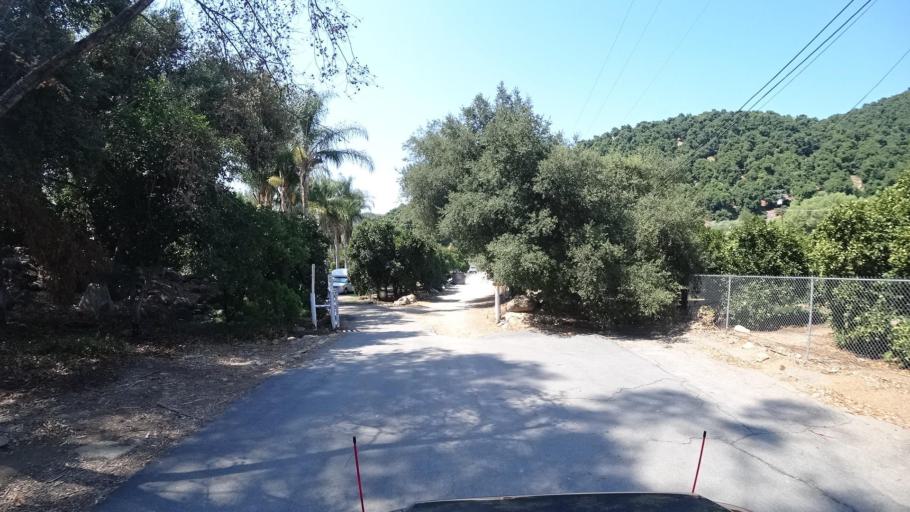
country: US
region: California
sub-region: San Diego County
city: Valley Center
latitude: 33.2919
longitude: -116.9612
